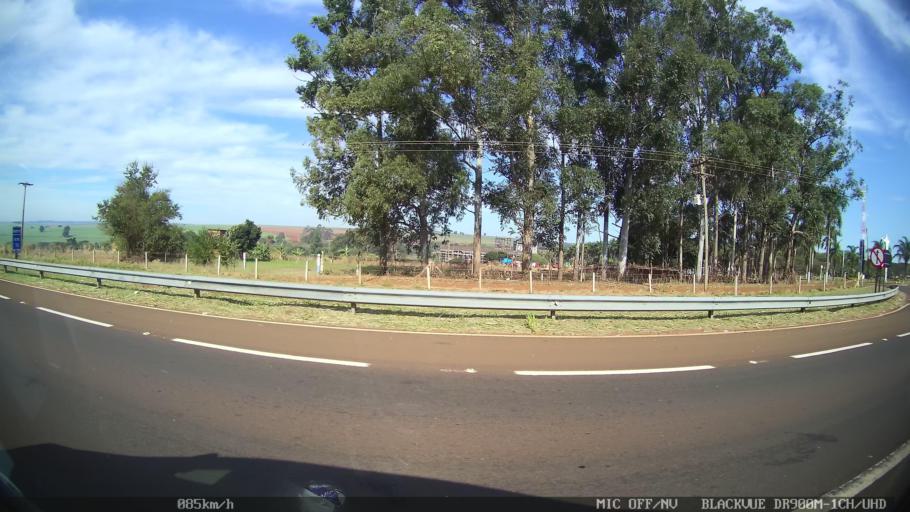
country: BR
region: Sao Paulo
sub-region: Americo Brasiliense
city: Americo Brasiliense
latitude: -21.7720
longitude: -48.0955
